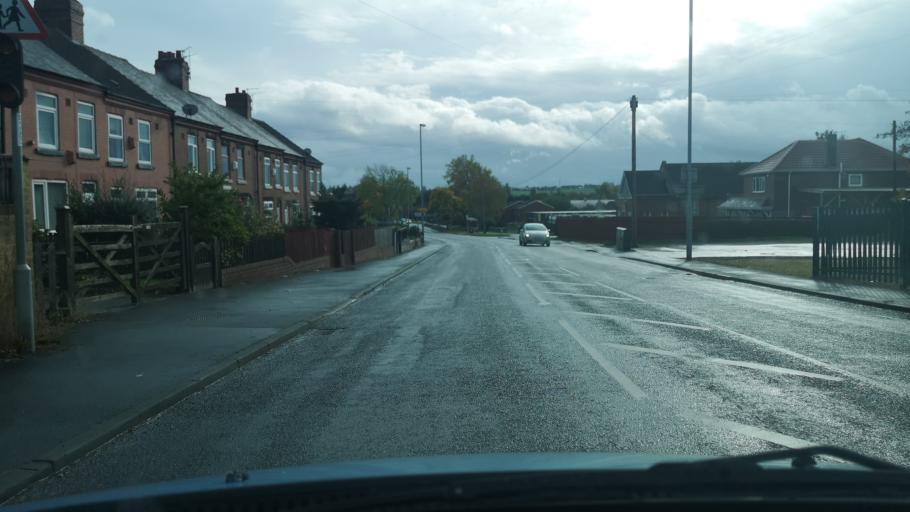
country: GB
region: England
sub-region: City and Borough of Wakefield
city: Fitzwilliam
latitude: 53.6314
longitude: -1.3742
